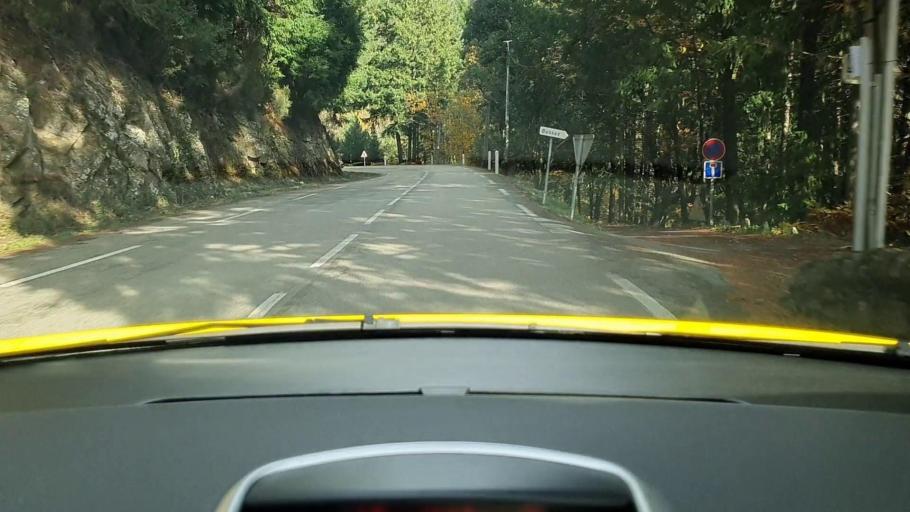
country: FR
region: Languedoc-Roussillon
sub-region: Departement du Gard
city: Saint-Jean-du-Gard
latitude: 44.1083
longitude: 3.8114
